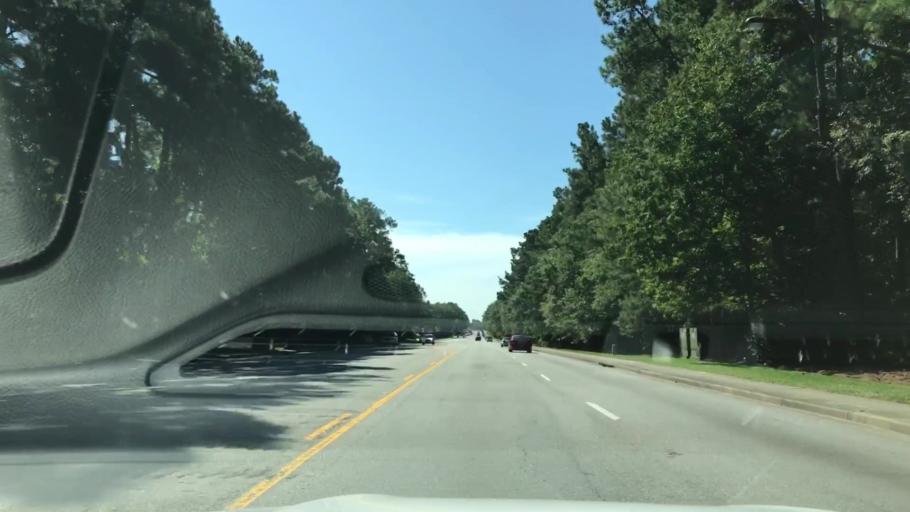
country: US
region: South Carolina
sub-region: Berkeley County
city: Goose Creek
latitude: 33.0202
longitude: -80.0526
